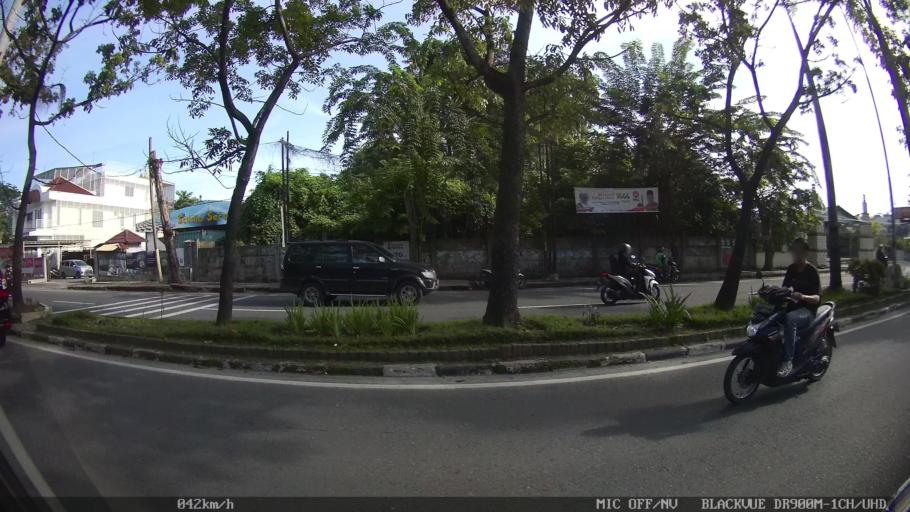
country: ID
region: North Sumatra
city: Medan
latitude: 3.6078
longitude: 98.6545
